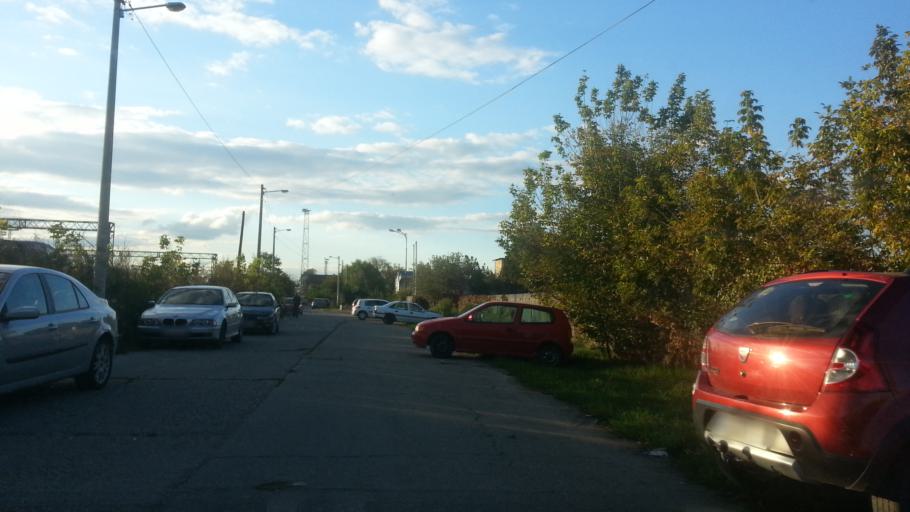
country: RS
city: Novi Banovci
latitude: 44.8974
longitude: 20.2755
